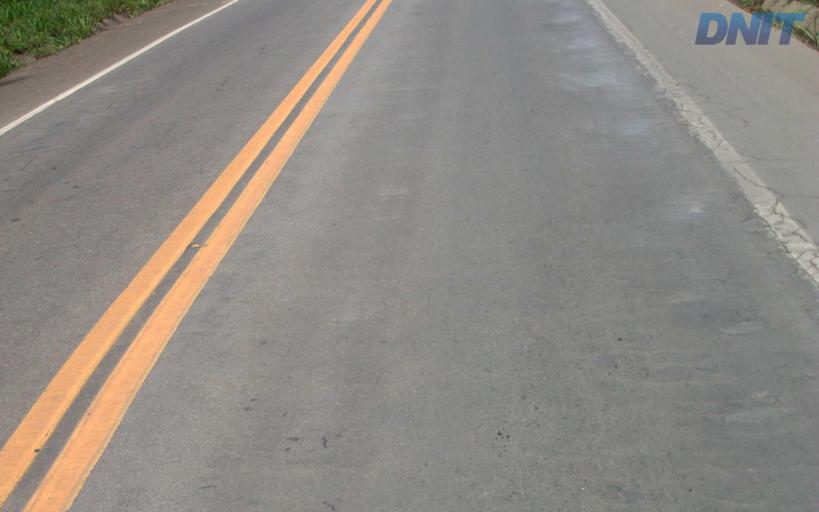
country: BR
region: Minas Gerais
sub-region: Ipaba
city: Ipaba
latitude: -19.3240
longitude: -42.4147
